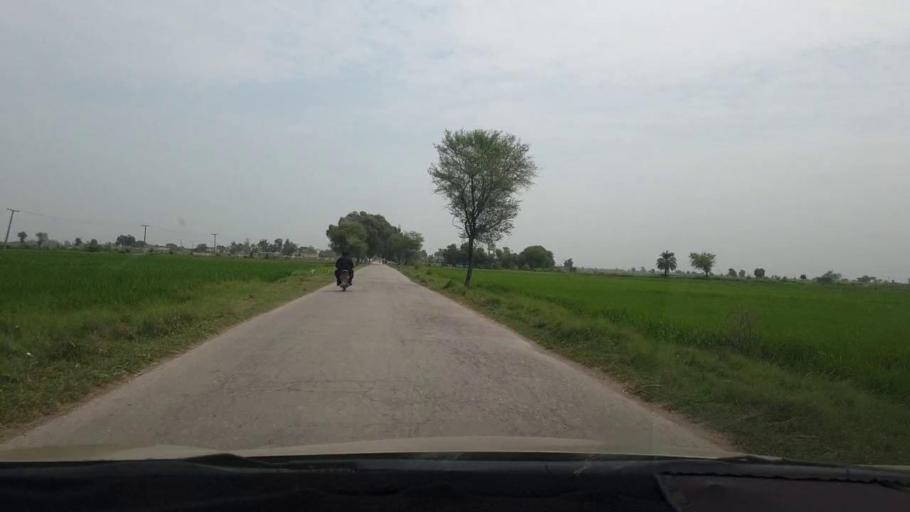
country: PK
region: Sindh
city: Ratodero
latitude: 27.7541
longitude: 68.3237
